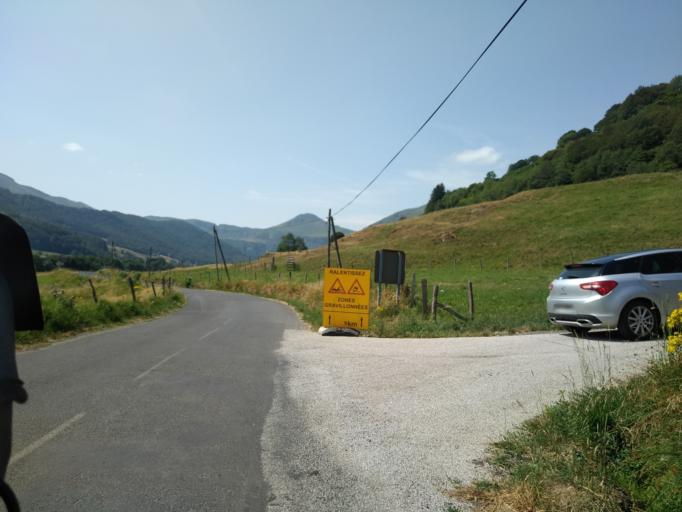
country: FR
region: Auvergne
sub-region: Departement du Cantal
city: Riom-es-Montagnes
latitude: 45.1561
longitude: 2.7027
